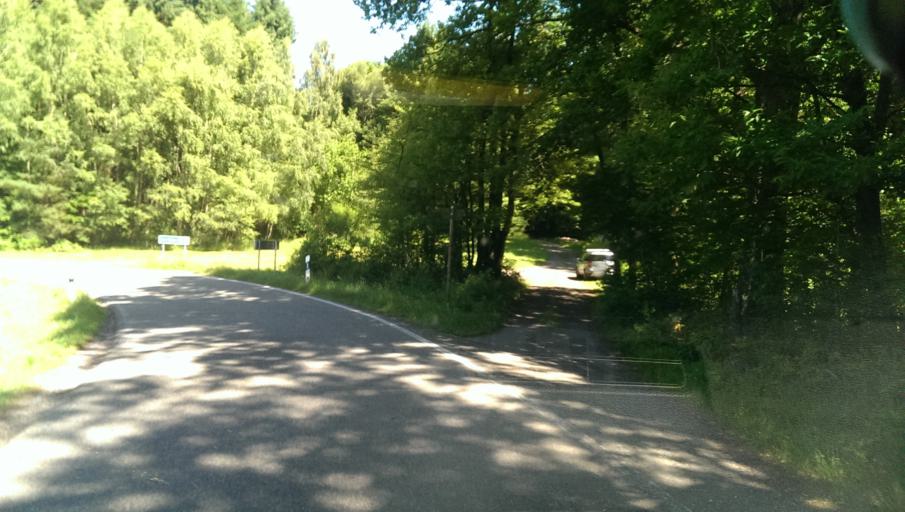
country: DE
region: Rheinland-Pfalz
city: Rumbach
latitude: 49.0846
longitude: 7.7953
